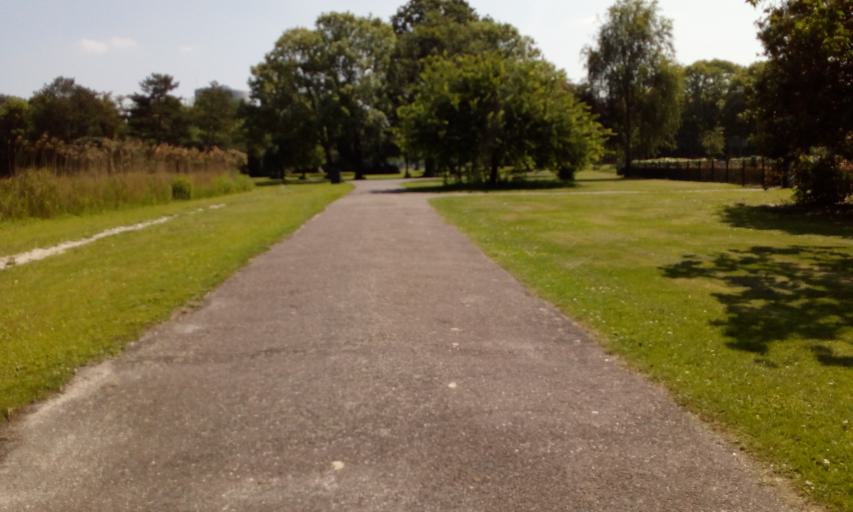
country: NL
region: South Holland
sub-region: Gemeente Den Haag
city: The Hague
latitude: 52.0572
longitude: 4.2870
